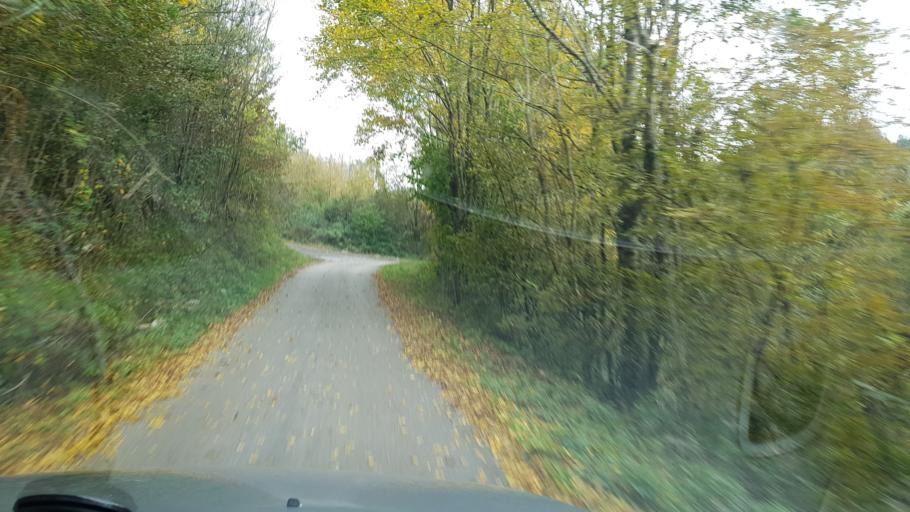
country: HR
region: Istarska
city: Buzet
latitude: 45.4412
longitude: 14.0485
